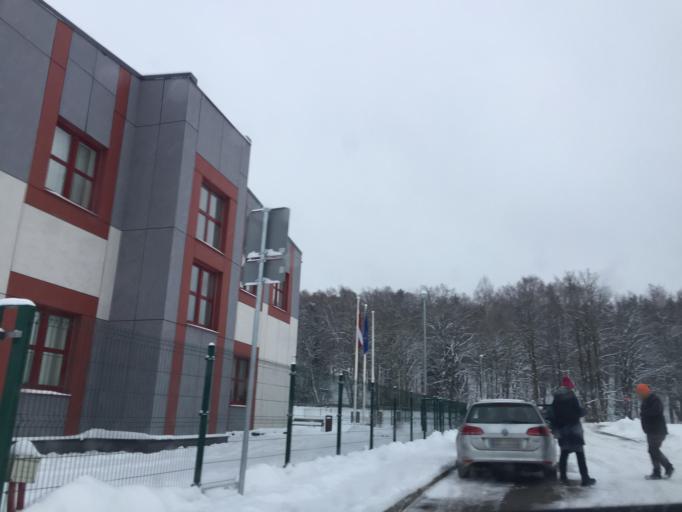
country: LV
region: Smiltene
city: Smiltene
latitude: 57.4295
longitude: 25.9009
